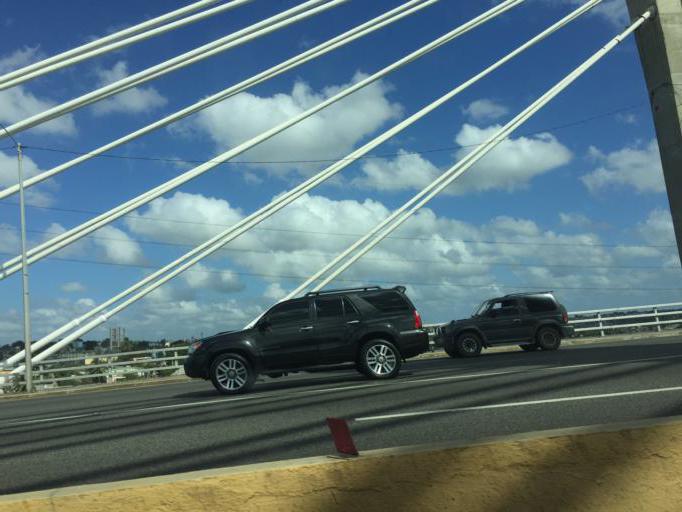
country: DO
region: Nacional
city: San Carlos
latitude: 18.4867
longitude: -69.8837
